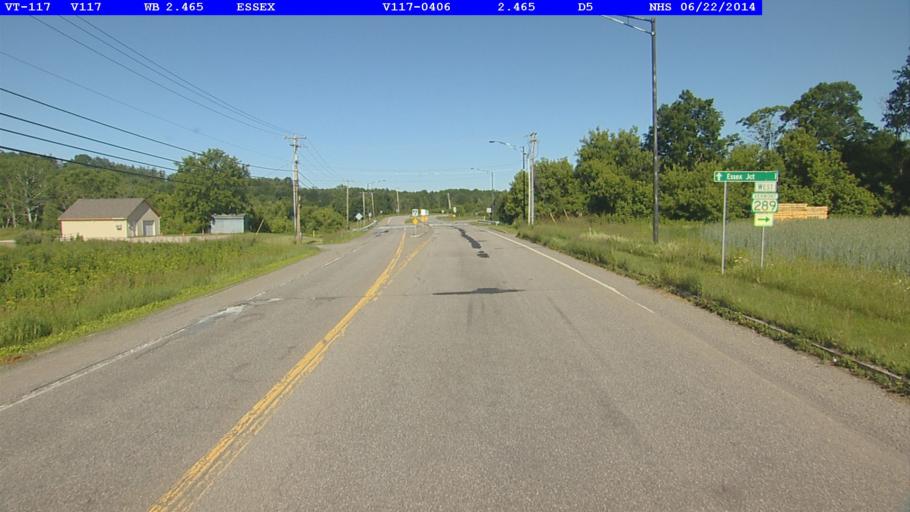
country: US
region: Vermont
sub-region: Chittenden County
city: Williston
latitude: 44.4798
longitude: -73.0652
